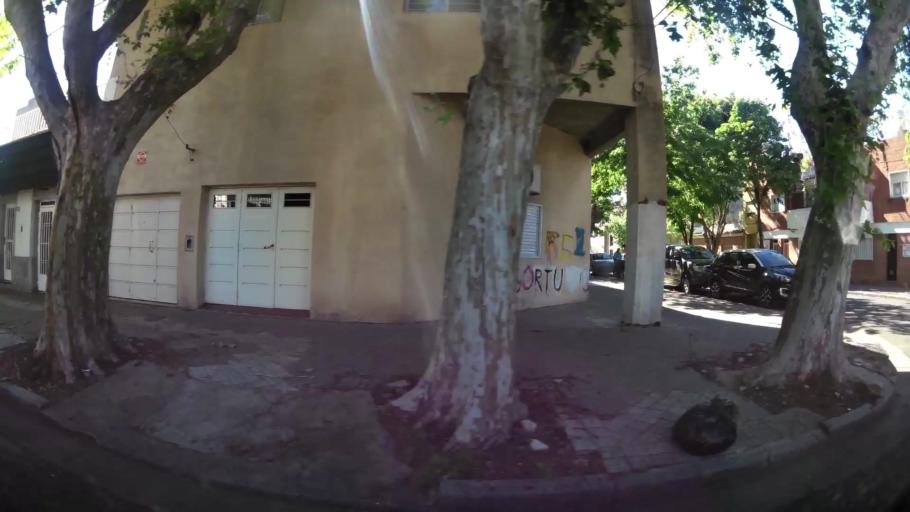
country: AR
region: Santa Fe
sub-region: Departamento de Rosario
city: Rosario
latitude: -32.9486
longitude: -60.6758
